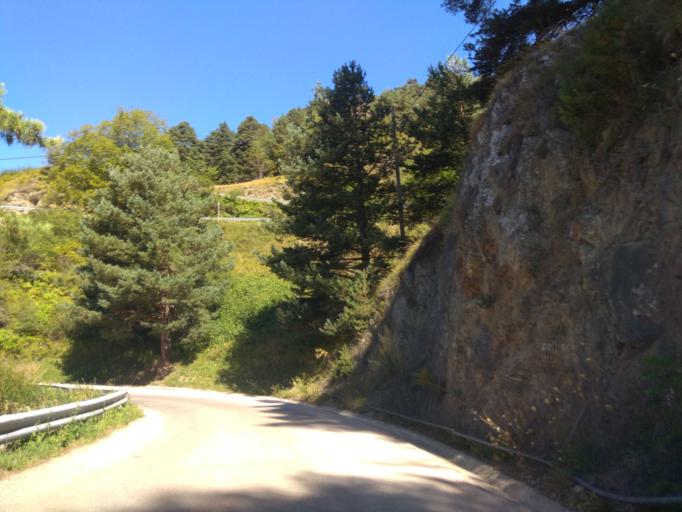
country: ES
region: Catalonia
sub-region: Provincia de Lleida
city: Les
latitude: 42.7511
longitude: 0.7162
